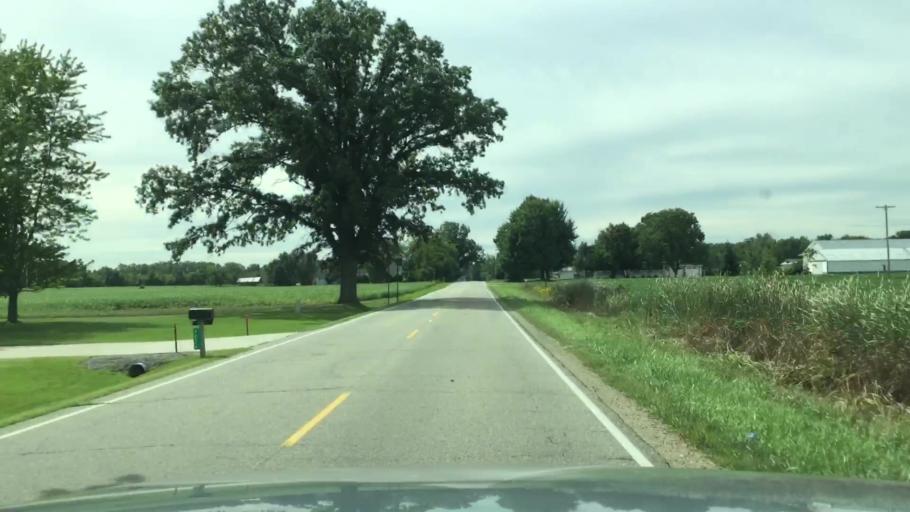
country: US
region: Michigan
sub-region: Genesee County
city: Montrose
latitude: 43.1146
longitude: -83.9880
